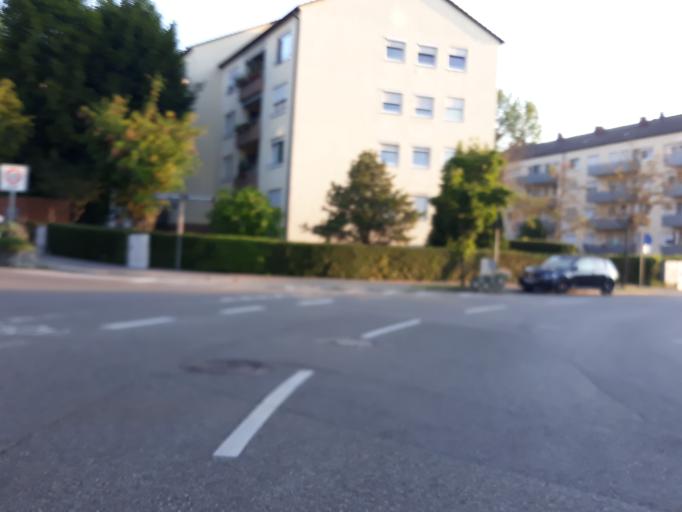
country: DE
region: Baden-Wuerttemberg
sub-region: Regierungsbezirk Stuttgart
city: Sindelfingen
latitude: 48.6985
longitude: 9.0192
